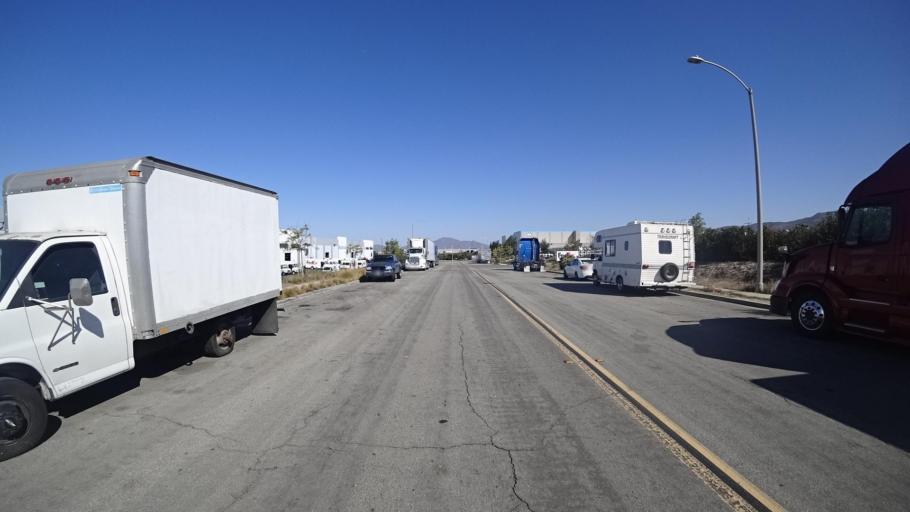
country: MX
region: Baja California
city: Tijuana
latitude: 32.5613
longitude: -116.9345
